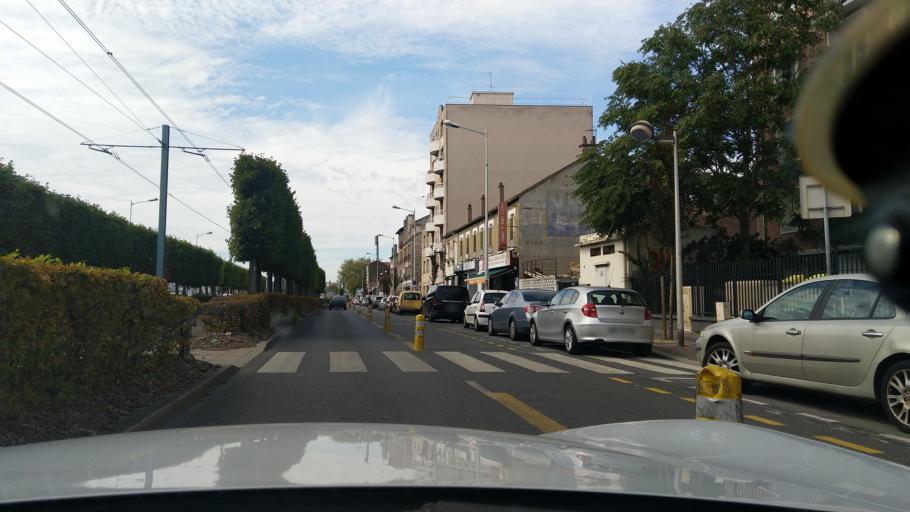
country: FR
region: Ile-de-France
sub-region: Departement de Seine-Saint-Denis
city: La Courneuve
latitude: 48.9240
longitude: 2.4039
